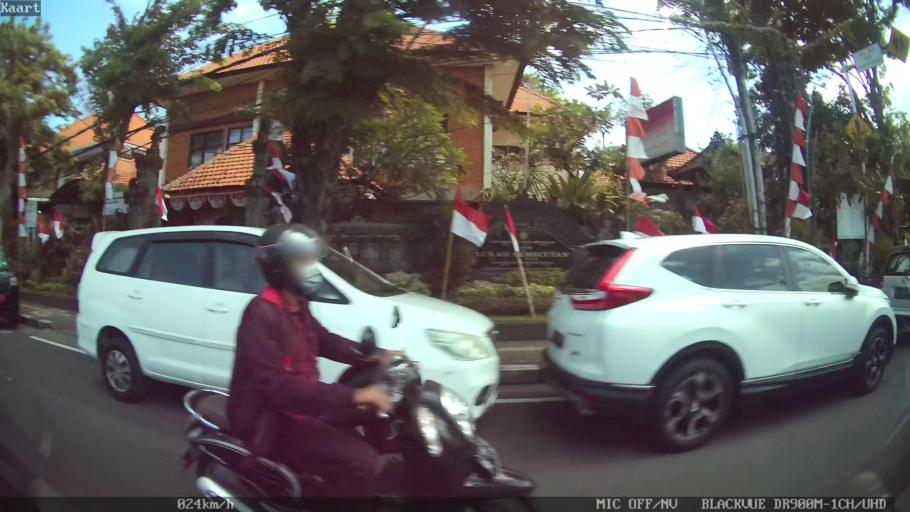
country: ID
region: Bali
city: Denpasar
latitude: -8.6600
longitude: 115.2091
